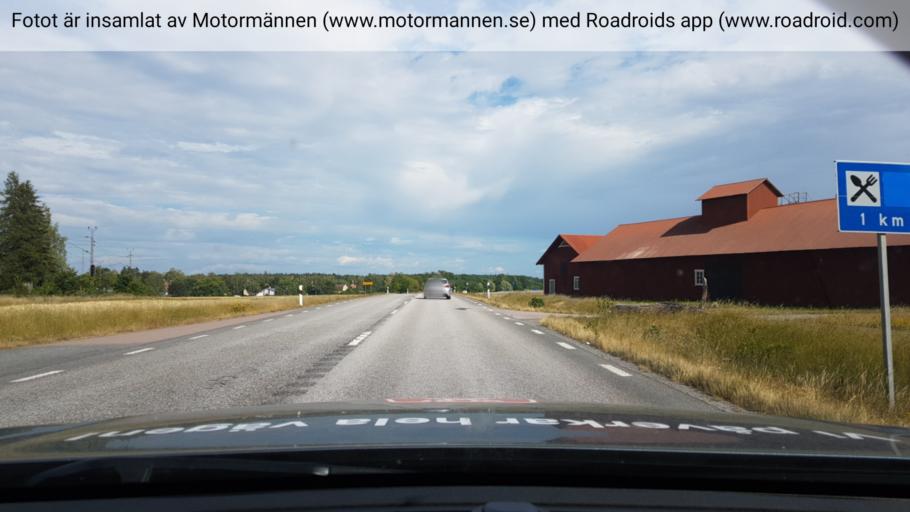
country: SE
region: Uppsala
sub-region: Enkopings Kommun
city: Orsundsbro
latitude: 59.8590
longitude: 17.4140
